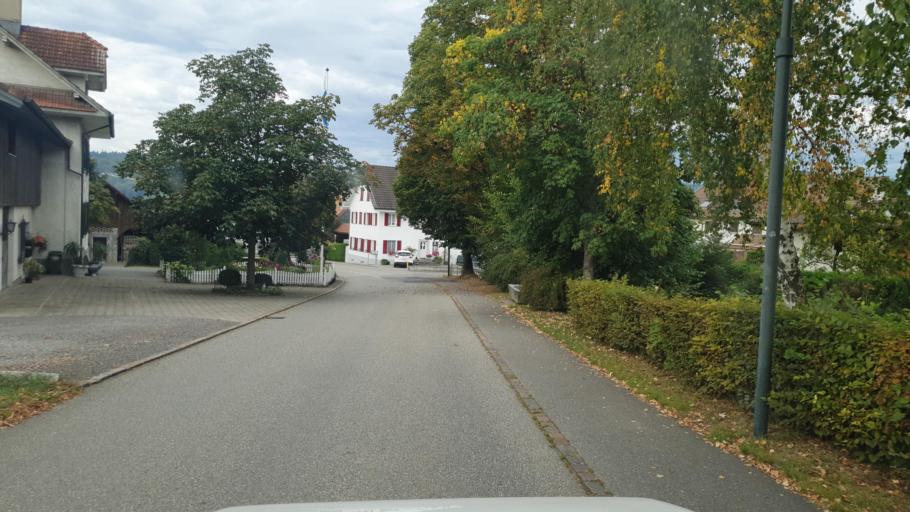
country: CH
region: Aargau
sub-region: Bezirk Lenzburg
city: Meisterschwanden
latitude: 47.2584
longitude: 8.2388
